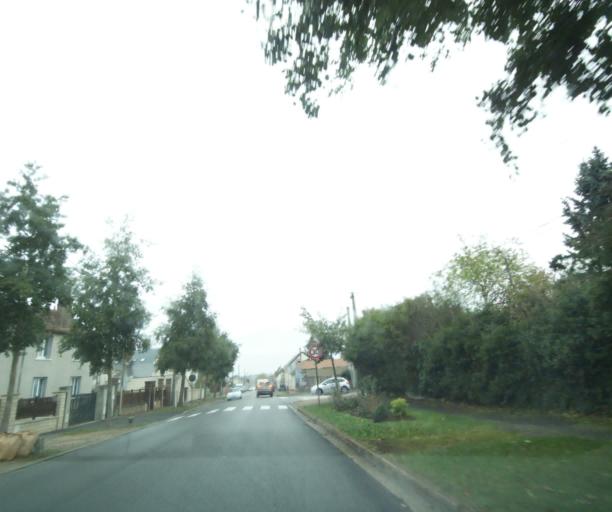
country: FR
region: Centre
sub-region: Departement d'Eure-et-Loir
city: Vernouillet
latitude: 48.7251
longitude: 1.3662
